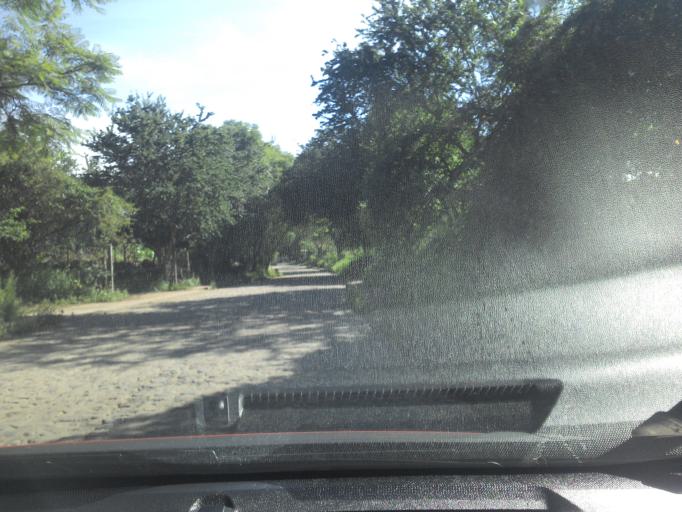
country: MX
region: Jalisco
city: Teuchitlan
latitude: 20.6923
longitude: -103.8437
